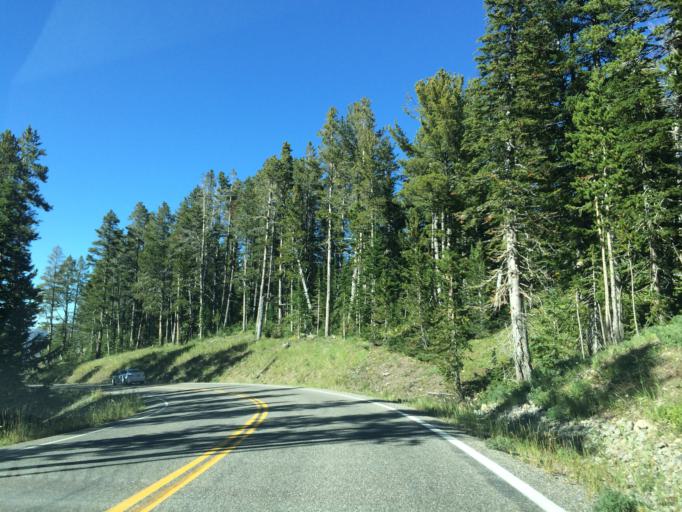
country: US
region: Montana
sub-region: Gallatin County
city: West Yellowstone
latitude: 44.8090
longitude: -110.4429
